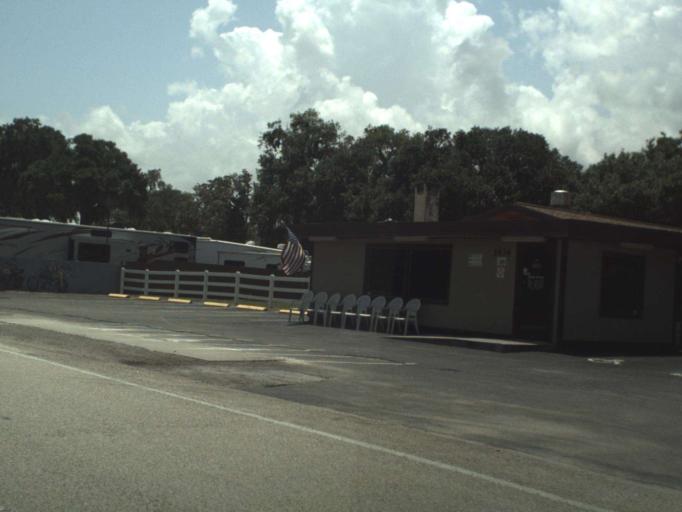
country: US
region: Florida
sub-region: Volusia County
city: Ponce Inlet
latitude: 29.1069
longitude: -80.9732
